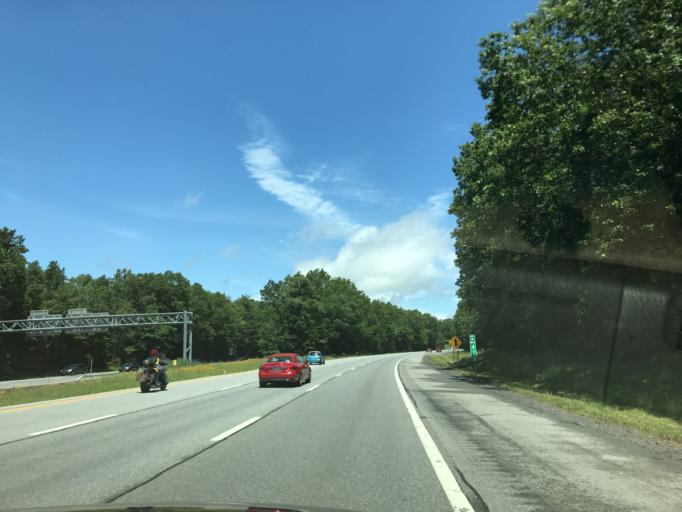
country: US
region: New York
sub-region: Warren County
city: West Glens Falls
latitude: 43.2383
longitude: -73.6921
